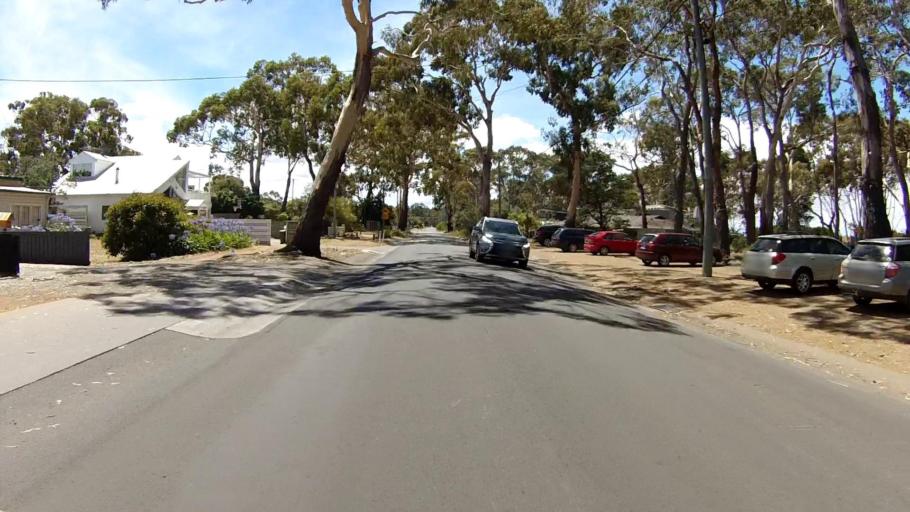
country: AU
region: Tasmania
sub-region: Clarence
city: Seven Mile Beach
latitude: -42.8596
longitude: 147.5067
